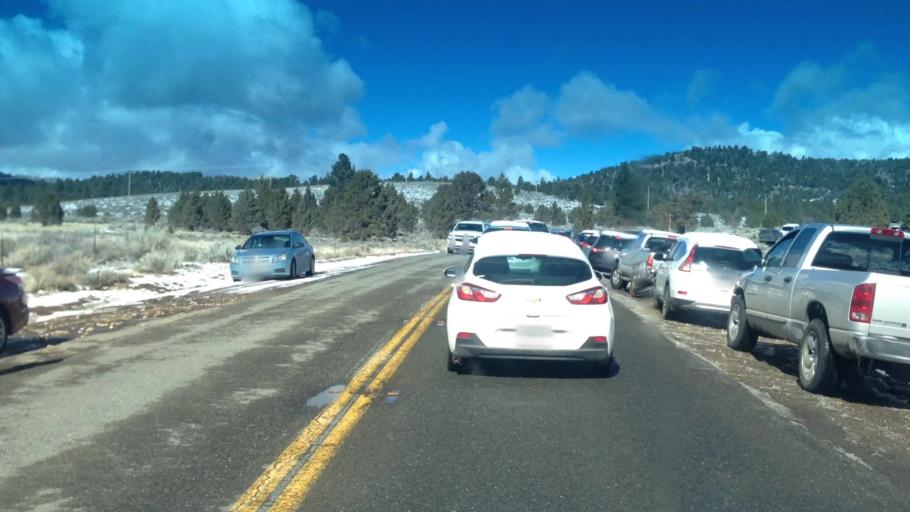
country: US
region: California
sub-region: San Bernardino County
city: Big Bear City
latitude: 34.2910
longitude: -116.8200
